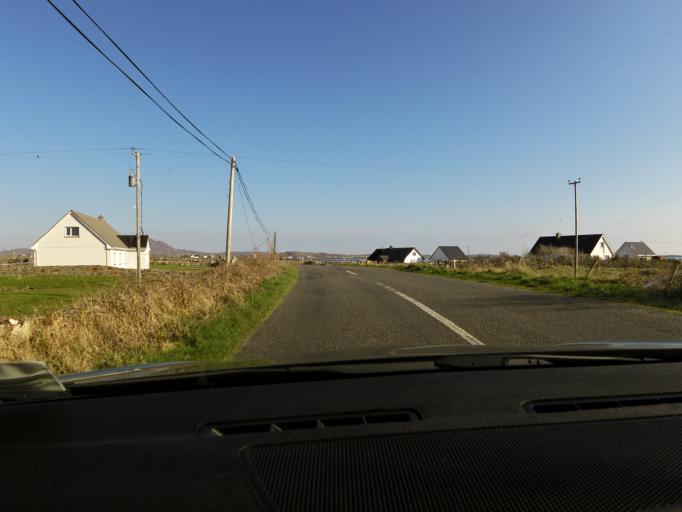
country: IE
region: Connaught
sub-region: County Galway
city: Clifden
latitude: 53.4172
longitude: -10.0585
